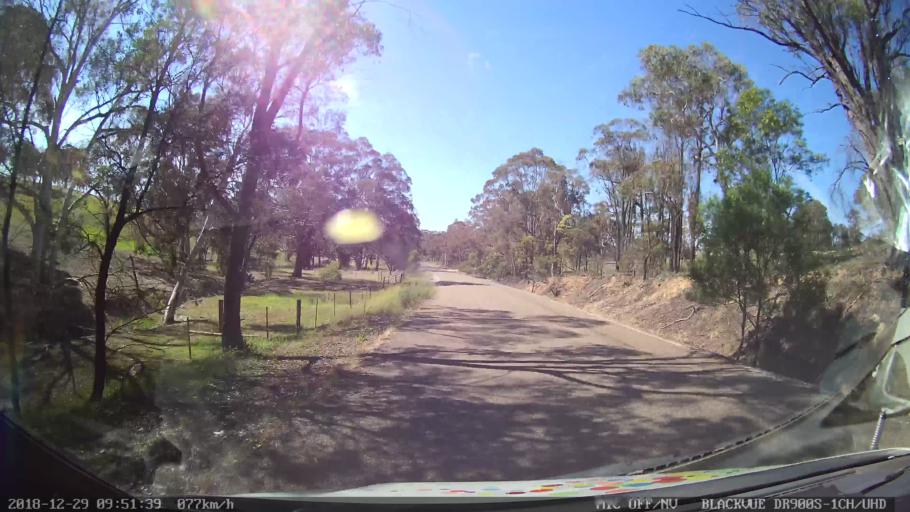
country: AU
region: New South Wales
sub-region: Goulburn Mulwaree
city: Goulburn
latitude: -34.7346
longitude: 149.4612
